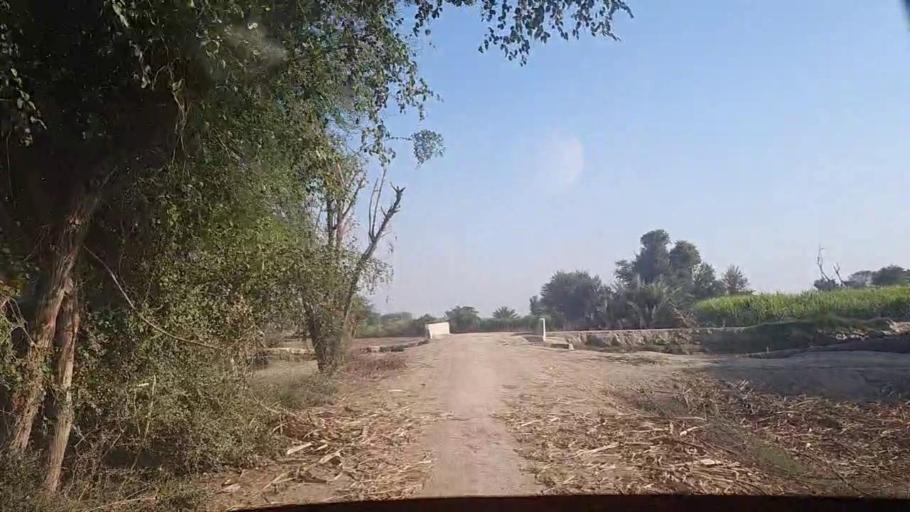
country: PK
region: Sindh
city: Gambat
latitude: 27.3781
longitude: 68.4677
